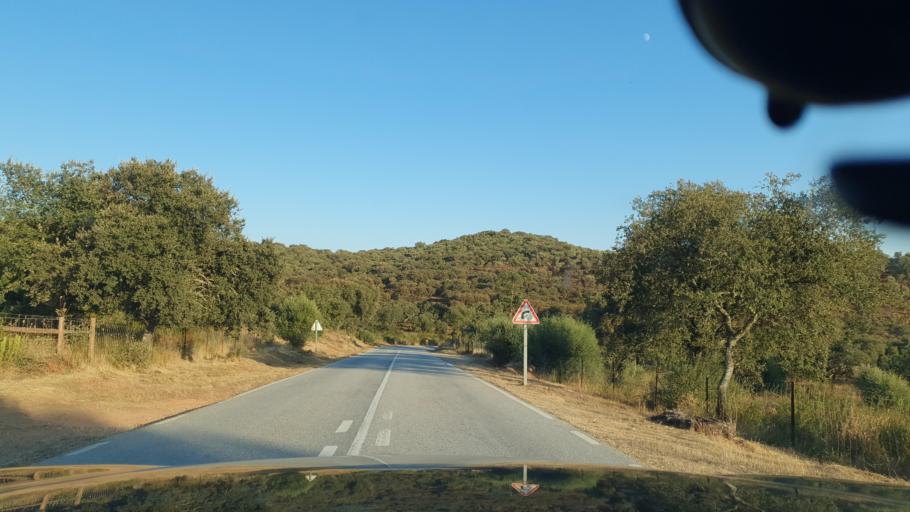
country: PT
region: Evora
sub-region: Estremoz
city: Estremoz
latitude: 38.9111
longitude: -7.6631
